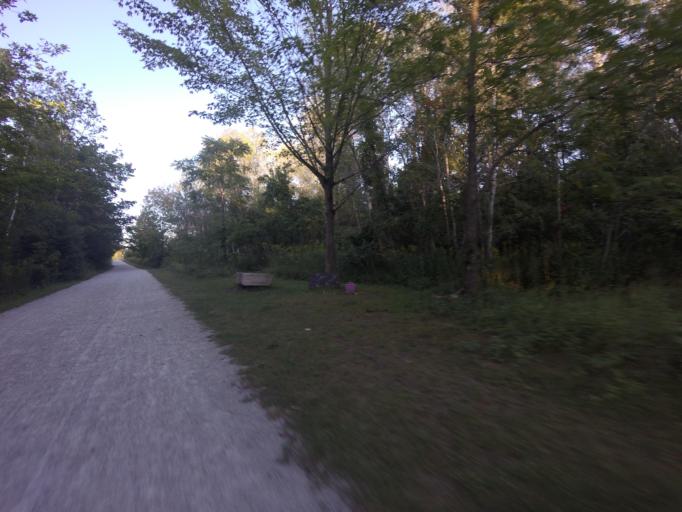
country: CA
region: Ontario
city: Brampton
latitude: 43.8724
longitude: -79.8602
